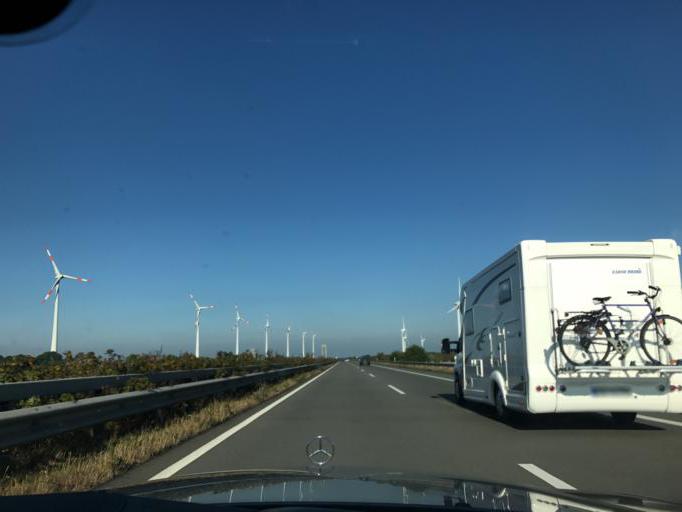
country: DE
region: Lower Saxony
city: Bunde
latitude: 53.1882
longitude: 7.2993
